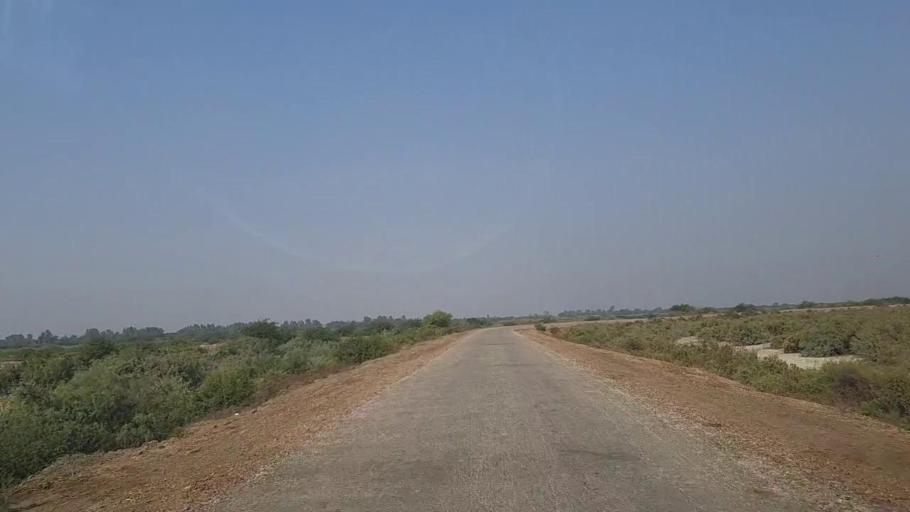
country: PK
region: Sindh
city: Keti Bandar
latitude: 24.2288
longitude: 67.6754
